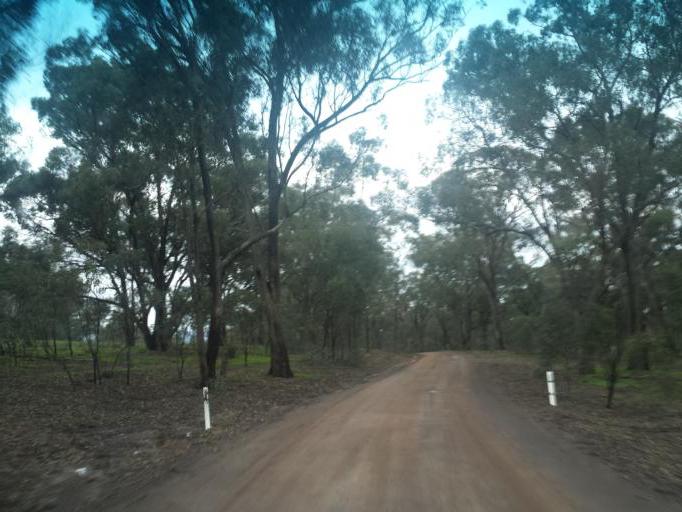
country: AU
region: Victoria
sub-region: Murrindindi
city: Kinglake West
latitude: -37.0271
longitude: 145.2084
